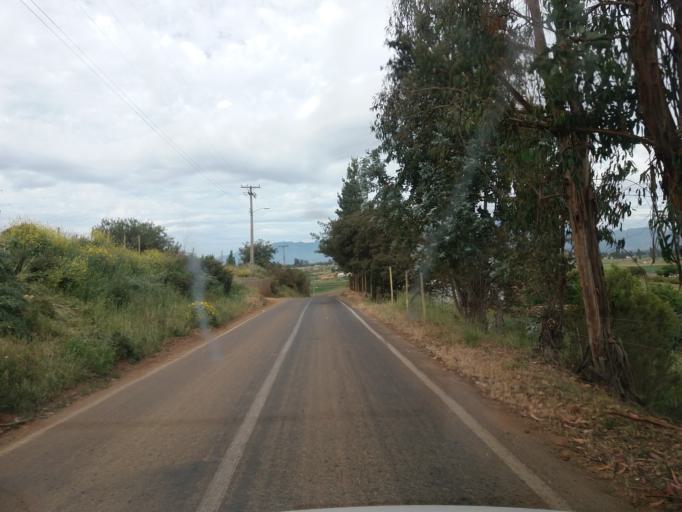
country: CL
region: Valparaiso
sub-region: Provincia de Quillota
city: Quillota
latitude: -32.9166
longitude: -71.3577
